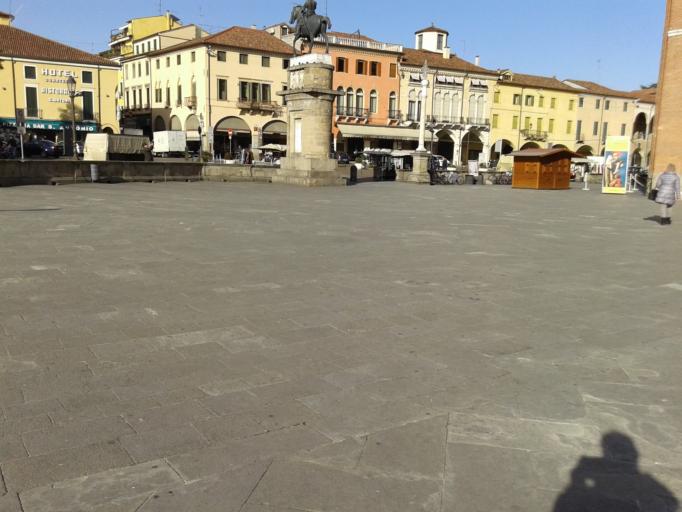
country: IT
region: Veneto
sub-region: Provincia di Padova
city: Padova
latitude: 45.4013
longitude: 11.8799
